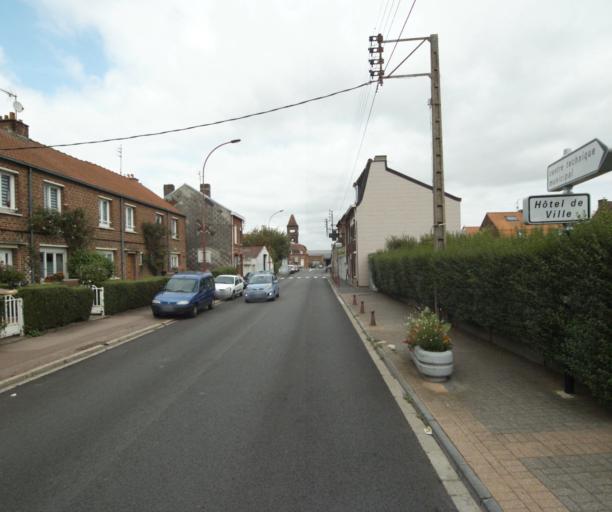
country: FR
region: Nord-Pas-de-Calais
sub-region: Departement du Nord
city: Leers
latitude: 50.6796
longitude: 3.2395
